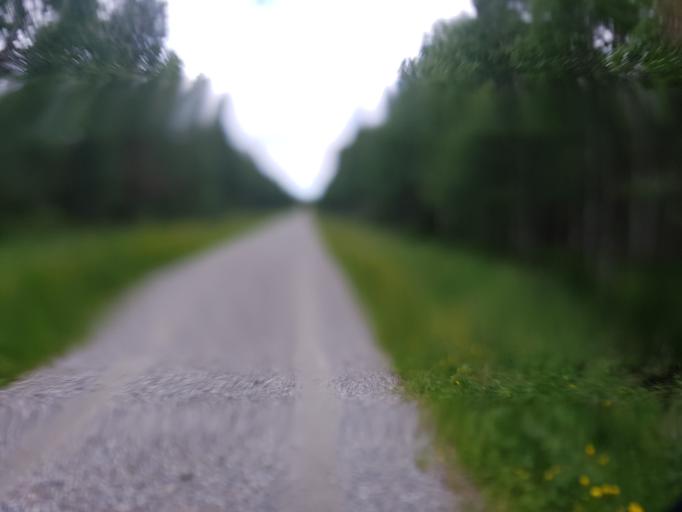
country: FI
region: Kainuu
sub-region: Kehys-Kainuu
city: Kuhmo
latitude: 64.4509
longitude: 29.6937
